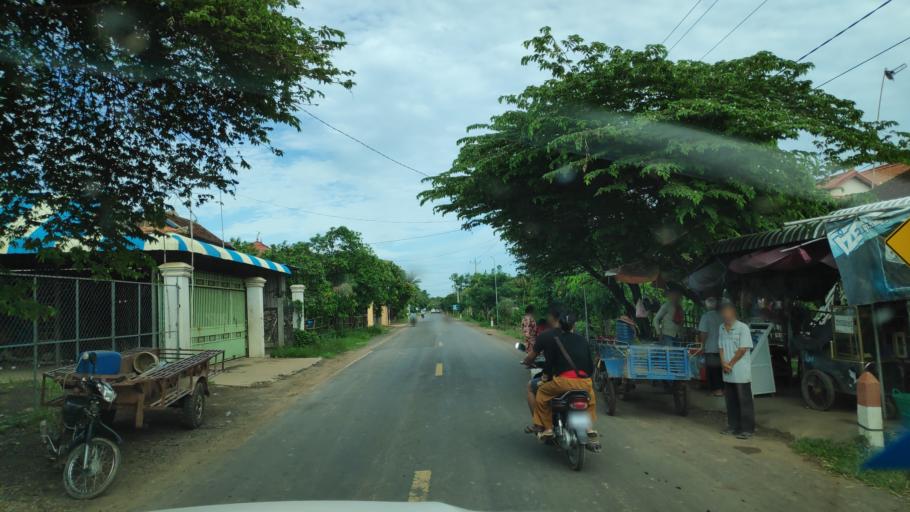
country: KH
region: Kampong Cham
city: Kampong Cham
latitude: 11.9475
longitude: 105.2416
